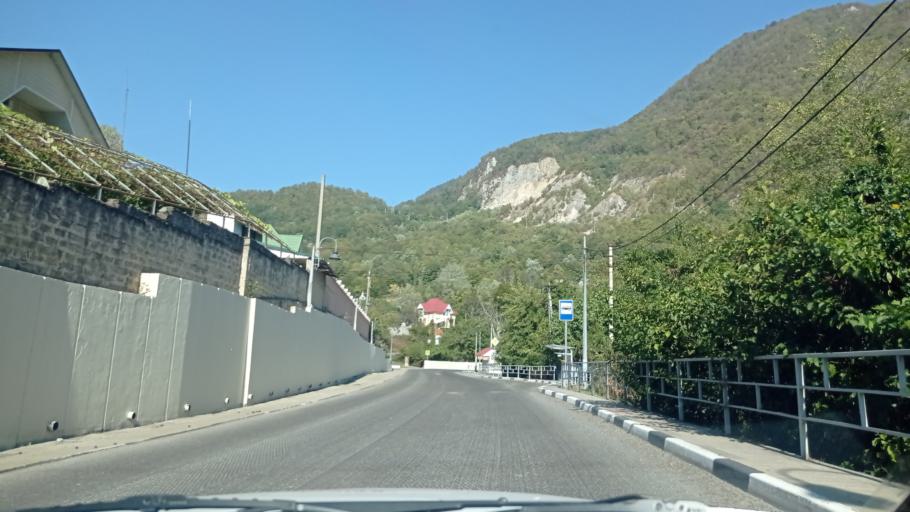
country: RU
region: Krasnodarskiy
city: Vysokoye
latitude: 43.5893
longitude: 40.0076
